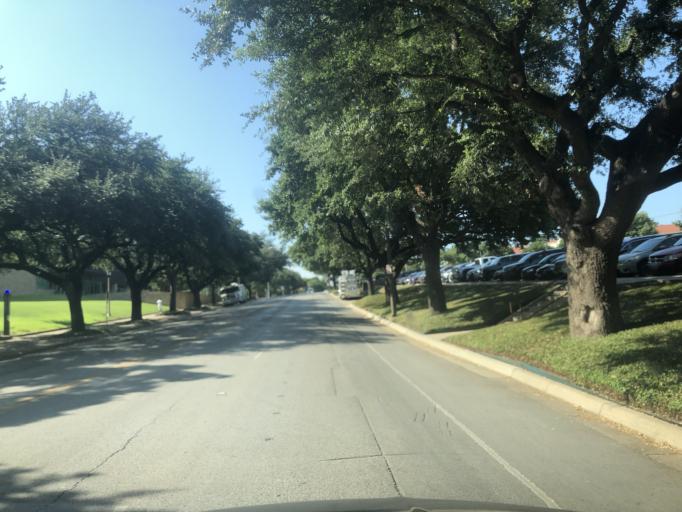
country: US
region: Texas
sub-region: Tarrant County
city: Fort Worth
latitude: 32.7085
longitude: -97.3651
